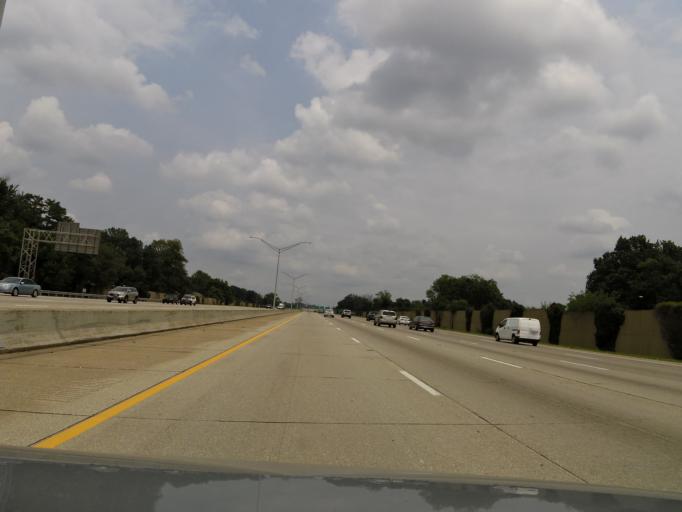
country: US
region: Kentucky
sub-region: Jefferson County
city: West Buechel
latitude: 38.2158
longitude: -85.6624
